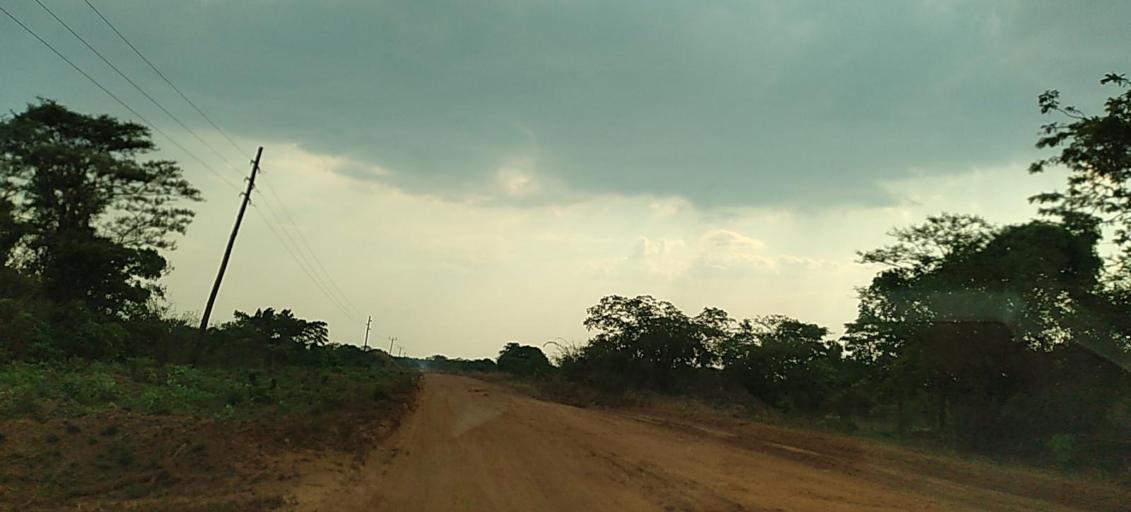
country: ZM
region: Copperbelt
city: Kalulushi
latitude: -12.9465
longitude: 27.9155
